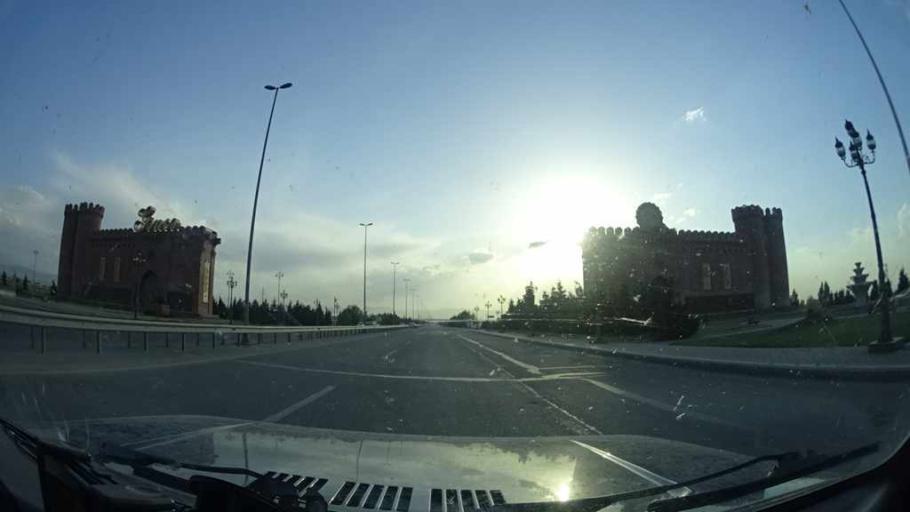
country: AZ
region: Samux
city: Samux
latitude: 40.6891
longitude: 46.4809
